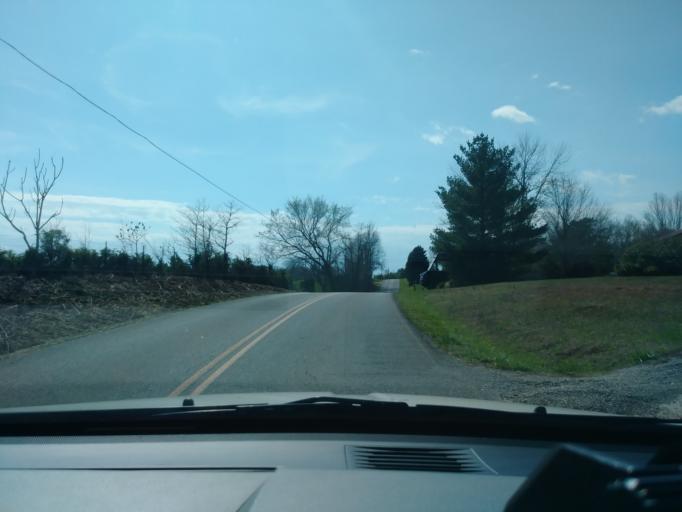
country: US
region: Tennessee
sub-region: Greene County
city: Greeneville
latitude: 36.0683
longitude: -82.7854
